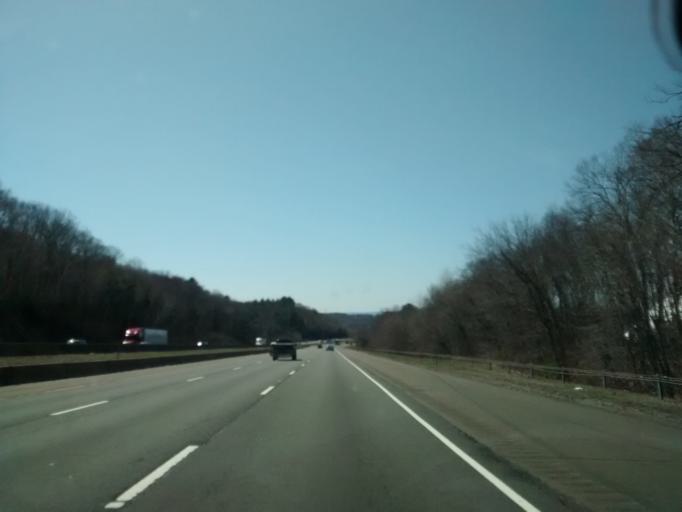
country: US
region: Connecticut
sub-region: Tolland County
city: Rockville
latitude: 41.8545
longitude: -72.4115
